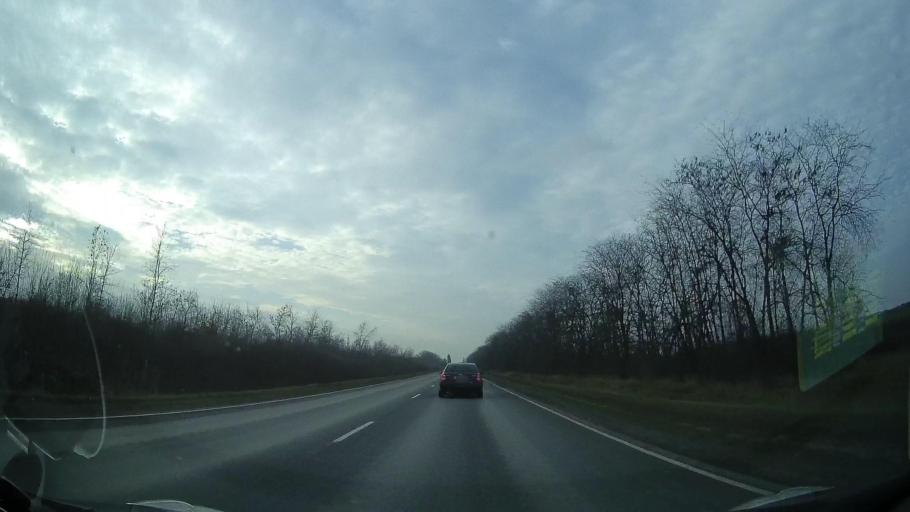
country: RU
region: Rostov
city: Ol'ginskaya
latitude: 47.1377
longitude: 40.0214
